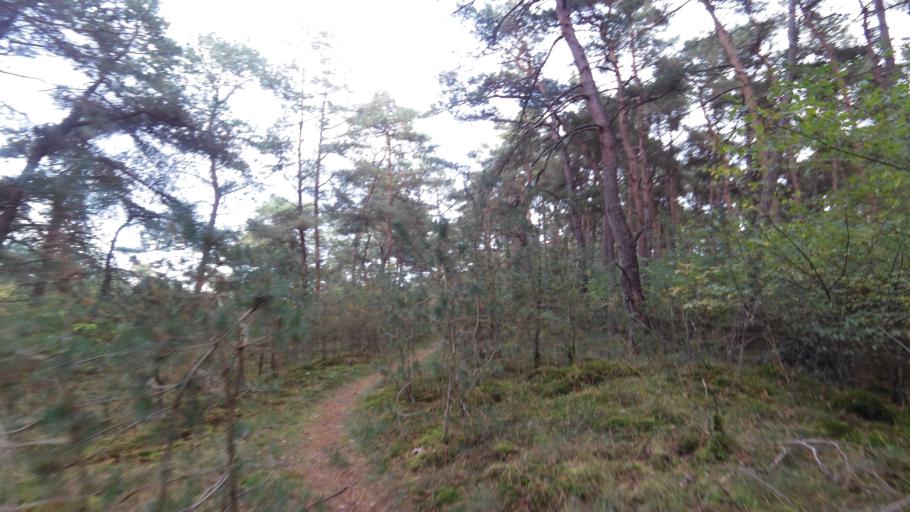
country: NL
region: Gelderland
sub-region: Gemeente Ede
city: Harskamp
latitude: 52.1627
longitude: 5.7586
